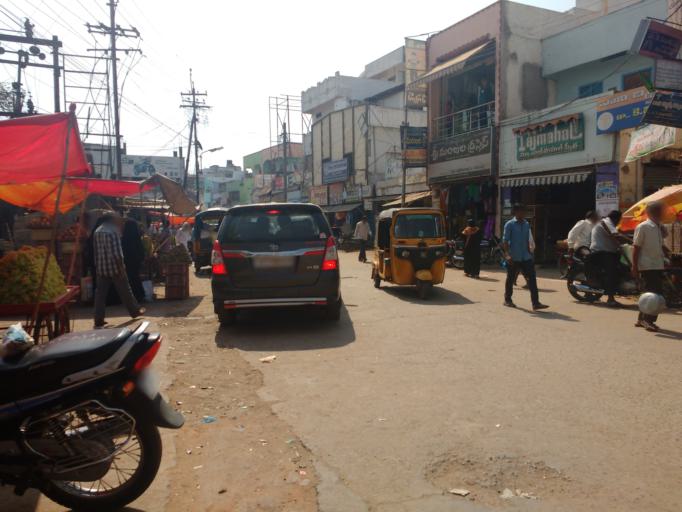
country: IN
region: Andhra Pradesh
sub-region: Kurnool
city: Nandyal
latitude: 15.4897
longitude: 78.4870
